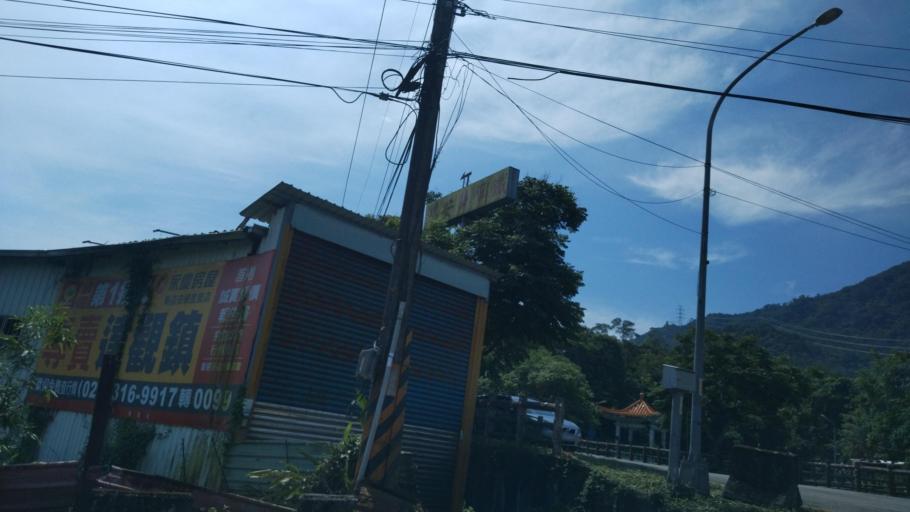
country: TW
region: Taipei
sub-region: Taipei
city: Banqiao
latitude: 24.9508
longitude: 121.5053
